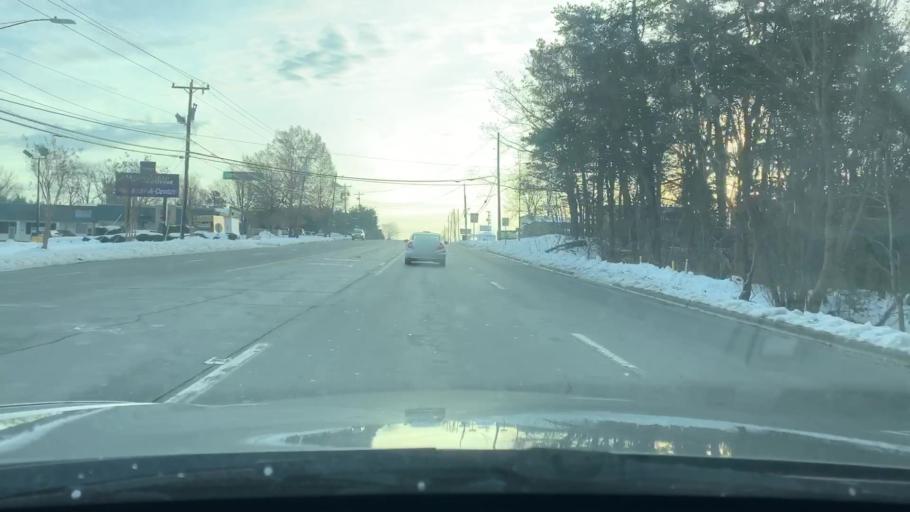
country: US
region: North Carolina
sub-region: Alamance County
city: Graham
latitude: 36.0930
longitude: -79.3955
